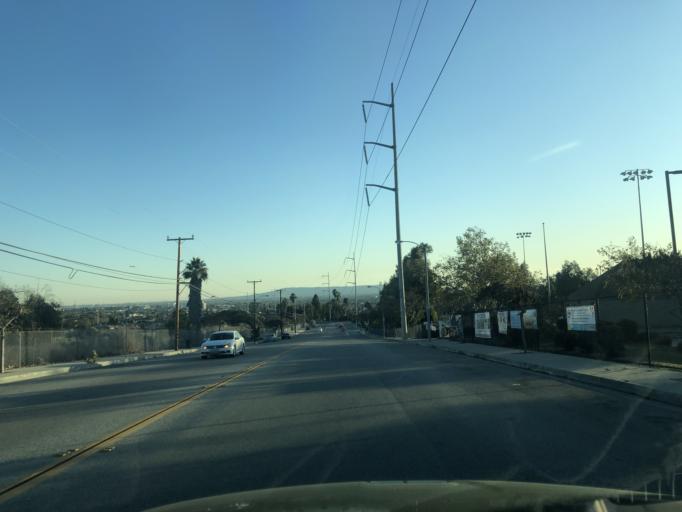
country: US
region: California
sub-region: Los Angeles County
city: Ladera Heights
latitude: 33.9926
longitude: -118.3636
